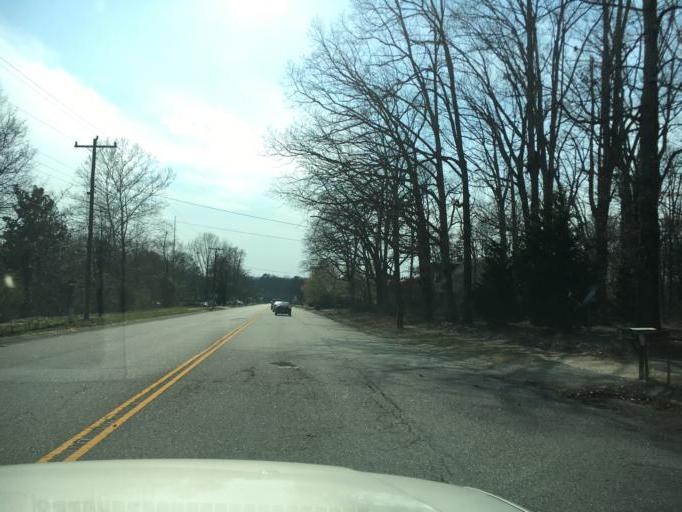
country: US
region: South Carolina
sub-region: Spartanburg County
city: Mayo
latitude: 35.1529
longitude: -81.8553
